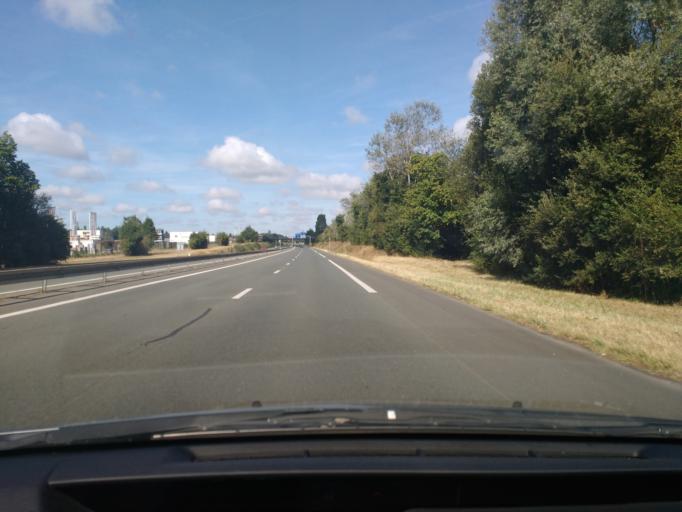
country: FR
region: Pays de la Loire
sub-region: Departement de Maine-et-Loire
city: Saint-Lambert-la-Potherie
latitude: 47.4649
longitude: -0.6595
